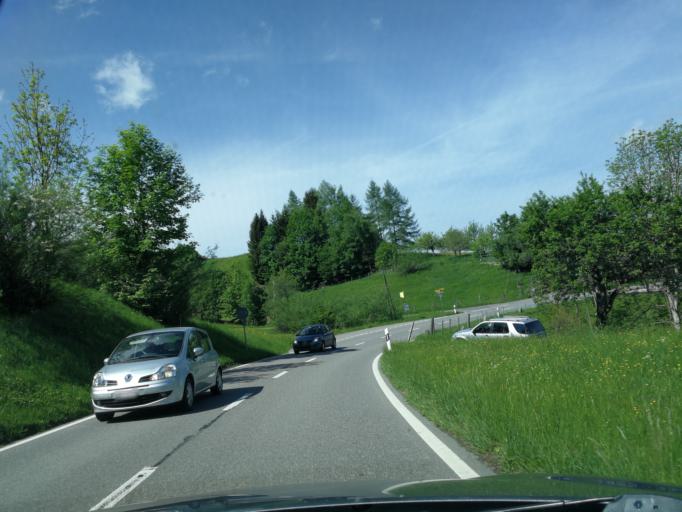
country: CH
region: Bern
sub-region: Bern-Mittelland District
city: Linden
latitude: 46.8380
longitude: 7.6677
